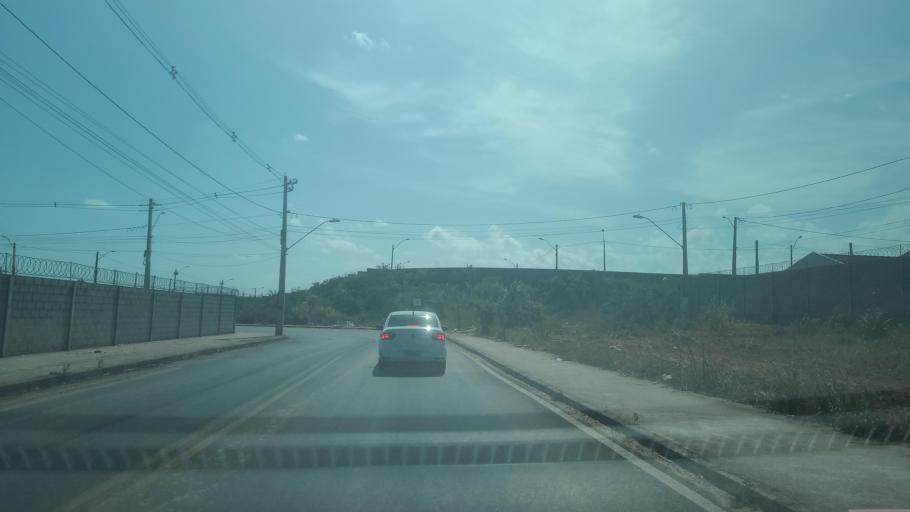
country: BR
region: Alagoas
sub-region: Satuba
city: Satuba
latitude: -9.5260
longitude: -35.7769
